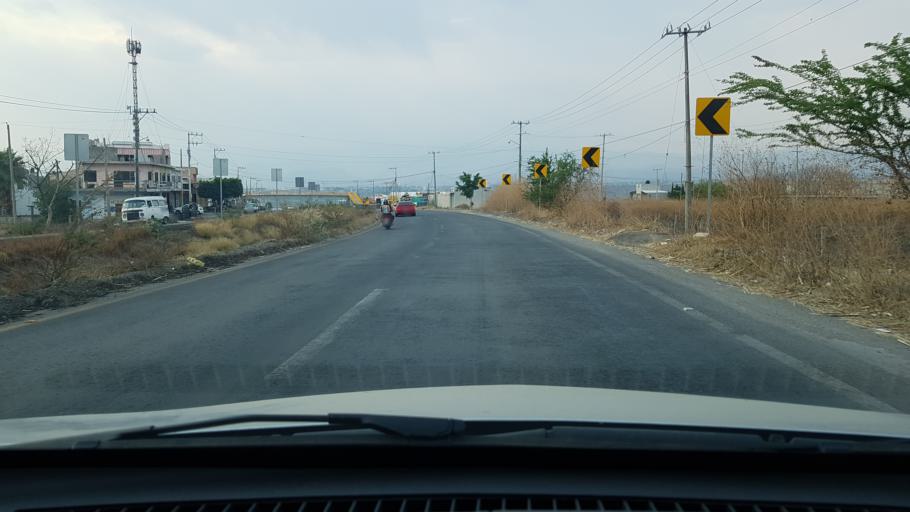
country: MX
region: Morelos
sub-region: Yecapixtla
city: Juan Morales
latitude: 18.8153
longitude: -98.9171
